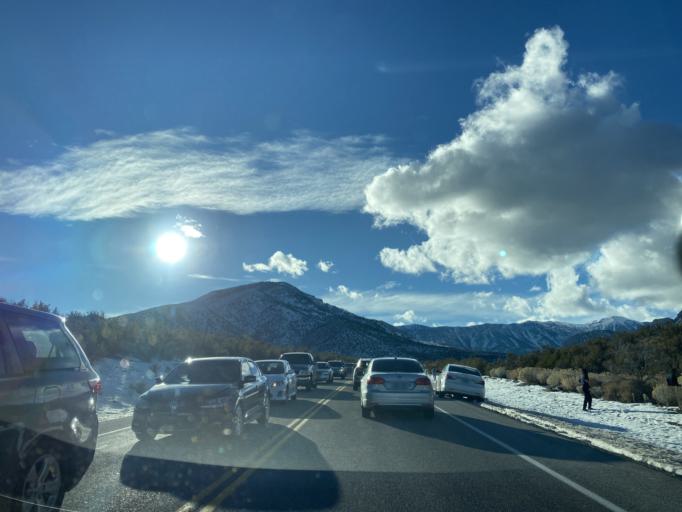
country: US
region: Nevada
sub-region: Clark County
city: Summerlin South
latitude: 36.2702
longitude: -115.5594
